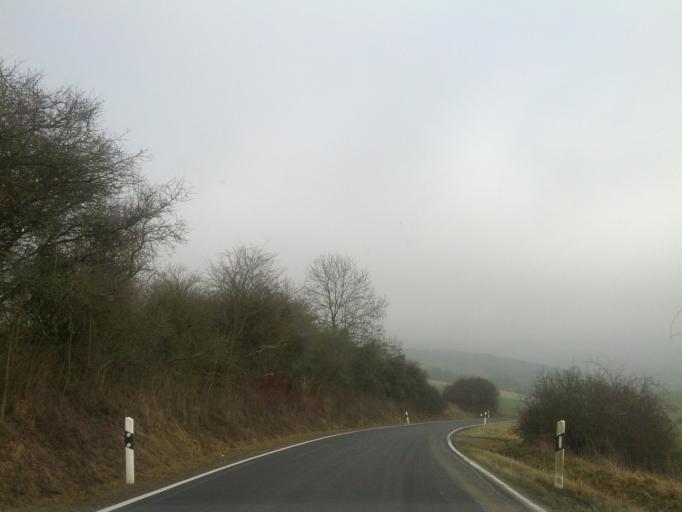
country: DE
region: Thuringia
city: Hallungen
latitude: 51.1224
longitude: 10.3135
